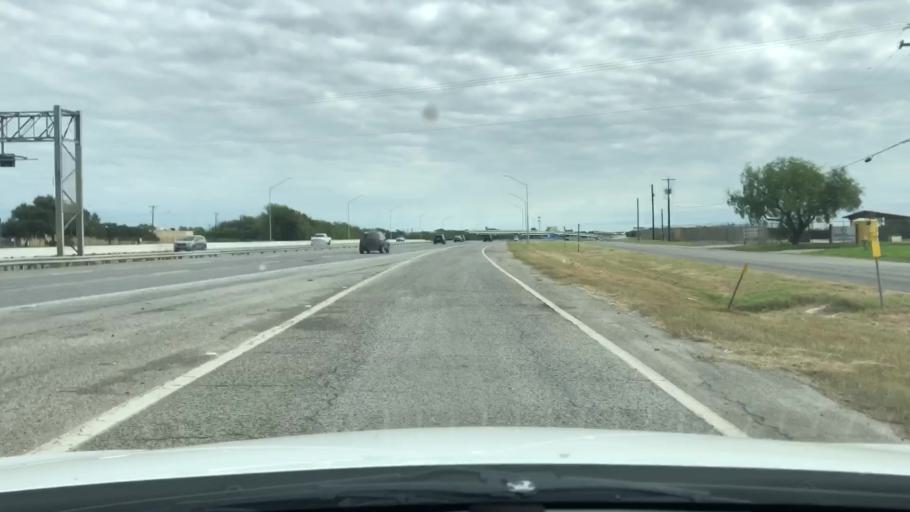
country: US
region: Texas
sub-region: Bexar County
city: Lackland Air Force Base
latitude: 29.4073
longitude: -98.5962
